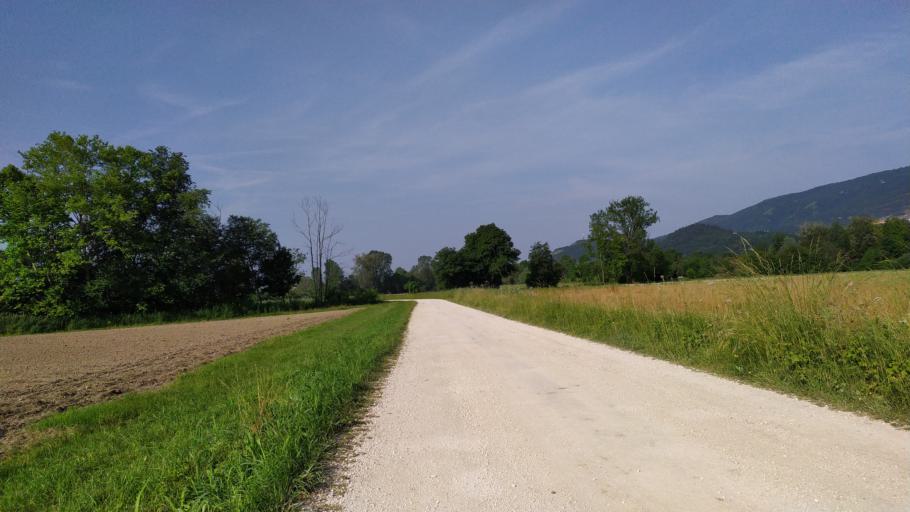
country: IT
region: Friuli Venezia Giulia
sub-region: Provincia di Pordenone
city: San Giovanni
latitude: 45.9992
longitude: 12.5027
